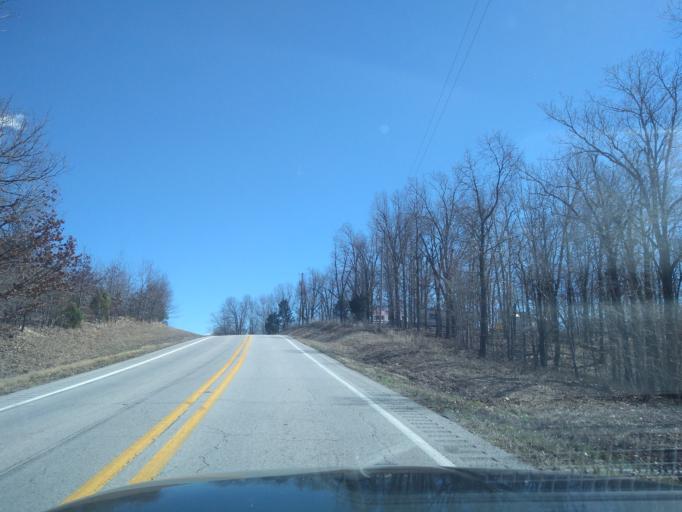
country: US
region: Arkansas
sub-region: Washington County
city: Farmington
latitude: 36.0886
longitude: -94.3300
